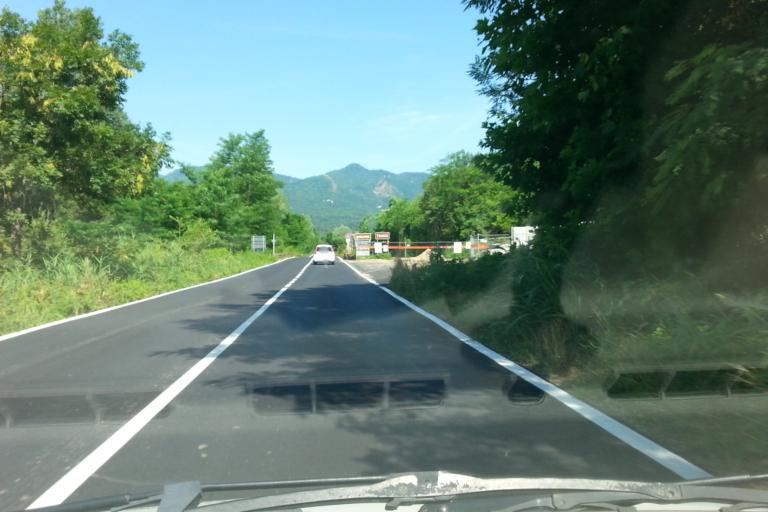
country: IT
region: Piedmont
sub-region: Provincia di Torino
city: Trana
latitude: 45.0496
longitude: 7.4026
